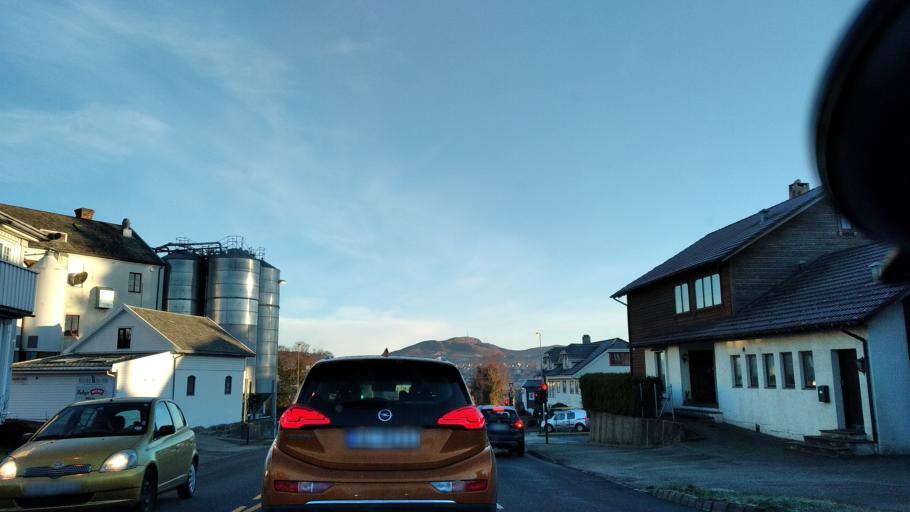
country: NO
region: Rogaland
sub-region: Sandnes
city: Sandnes
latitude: 58.8525
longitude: 5.7245
